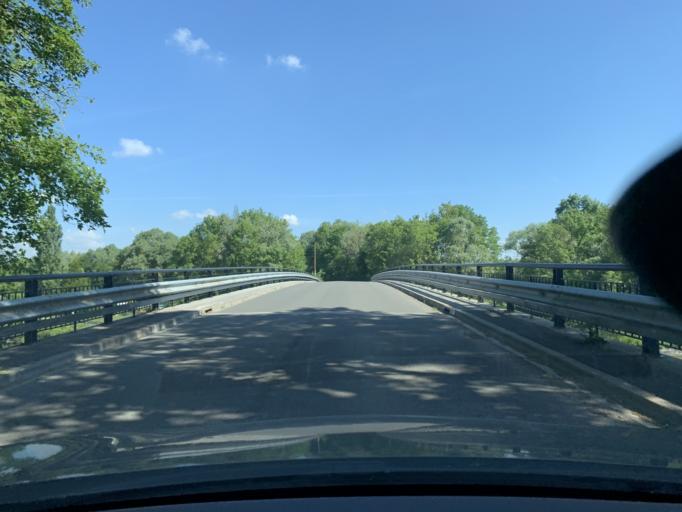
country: FR
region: Nord-Pas-de-Calais
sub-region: Departement du Pas-de-Calais
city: Oisy-le-Verger
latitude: 50.2622
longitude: 3.1405
